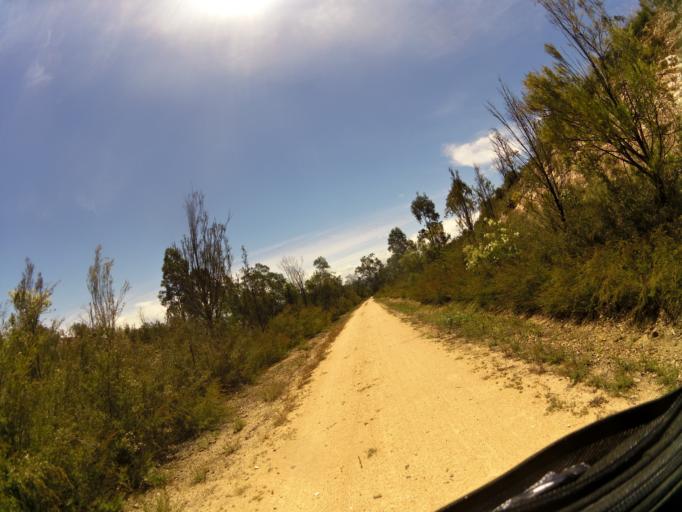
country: AU
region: Victoria
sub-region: East Gippsland
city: Lakes Entrance
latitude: -37.7282
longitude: 147.8528
